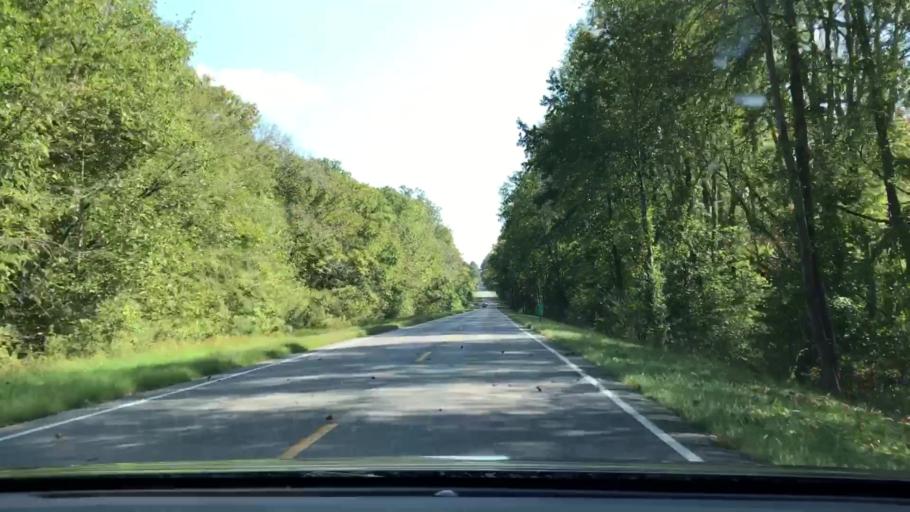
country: US
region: Kentucky
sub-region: Marshall County
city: Benton
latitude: 36.7645
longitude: -88.2253
